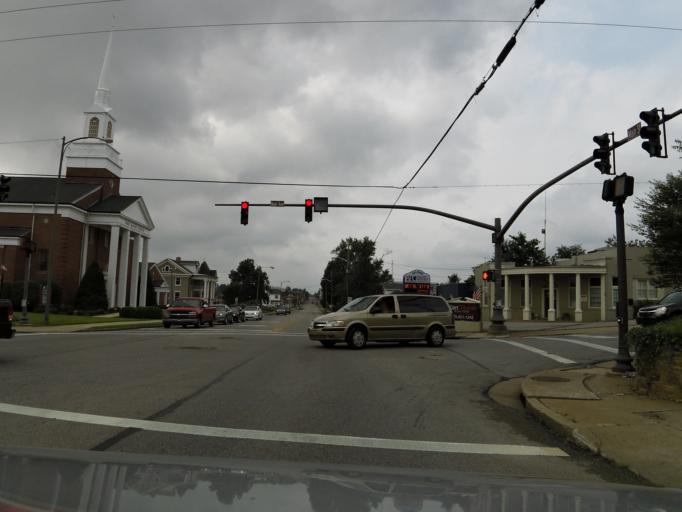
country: US
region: Kentucky
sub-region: Hopkins County
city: Madisonville
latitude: 37.3332
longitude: -87.4981
